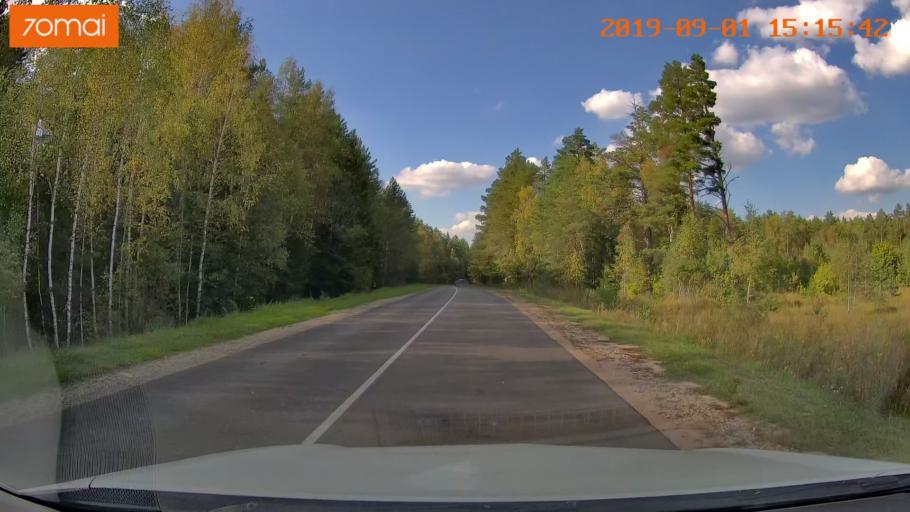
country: RU
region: Kaluga
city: Maloyaroslavets
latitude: 54.8800
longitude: 36.5341
